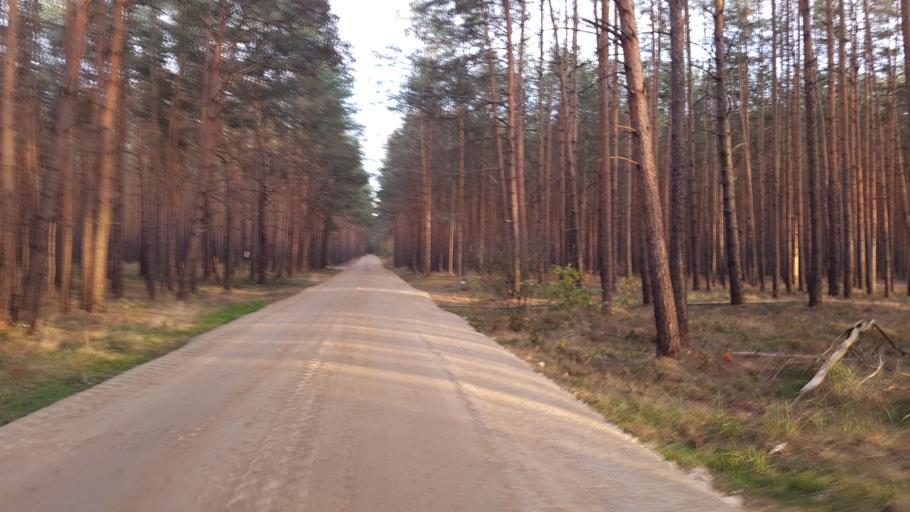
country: DE
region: Brandenburg
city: Trobitz
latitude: 51.5607
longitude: 13.4261
